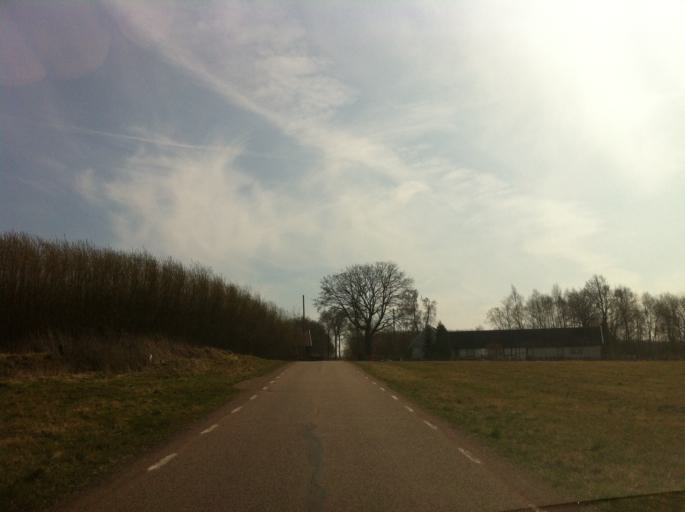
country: SE
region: Skane
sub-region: Klippans Kommun
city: Ljungbyhed
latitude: 55.9952
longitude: 13.2320
